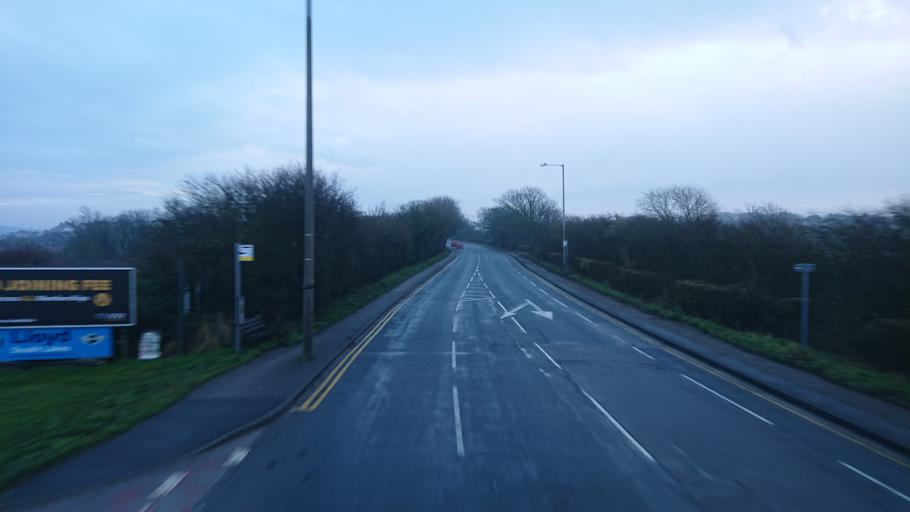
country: GB
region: England
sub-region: Lancashire
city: Morecambe
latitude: 54.0862
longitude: -2.8248
